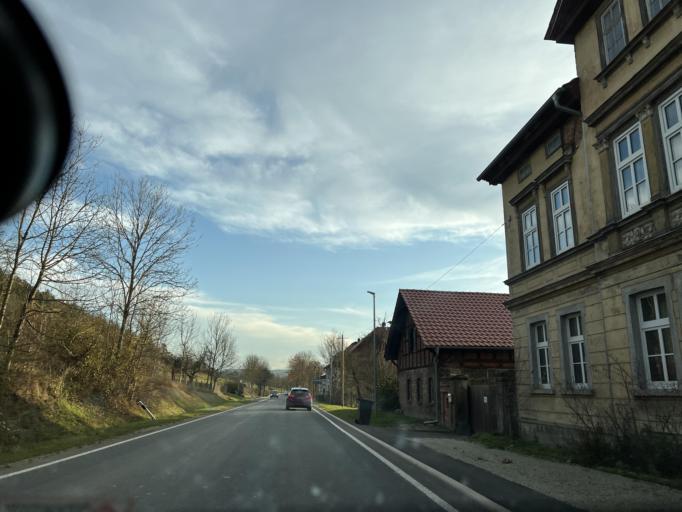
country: DE
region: Thuringia
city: Barchfeld
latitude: 50.8292
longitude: 11.1816
